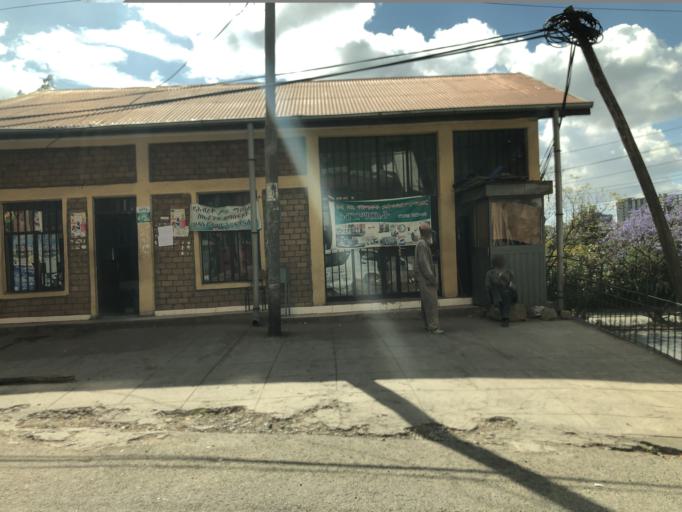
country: ET
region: Adis Abeba
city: Addis Ababa
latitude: 8.9963
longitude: 38.7790
